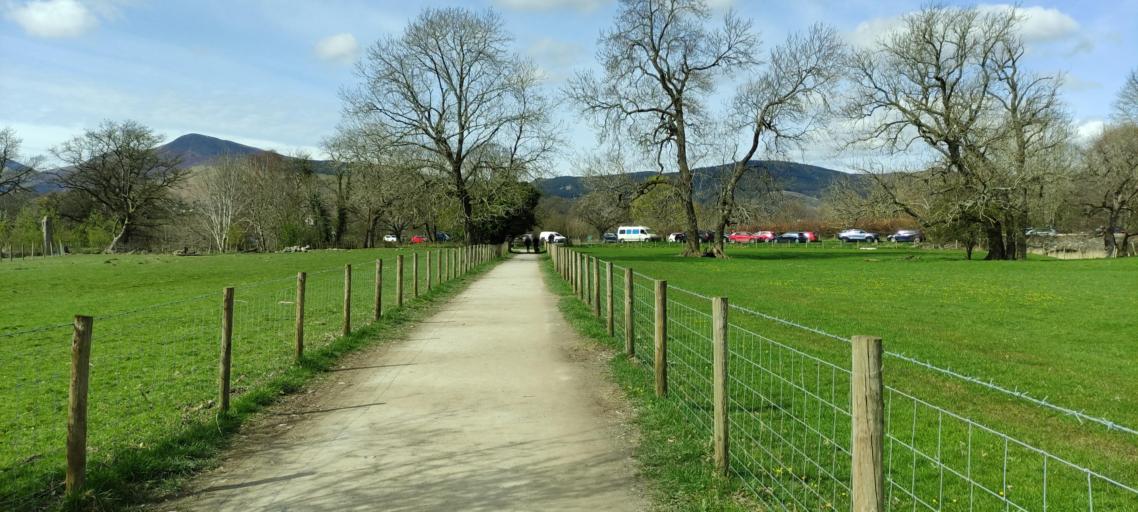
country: GB
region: England
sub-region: Cumbria
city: Keswick
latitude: 54.6047
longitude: -3.1534
